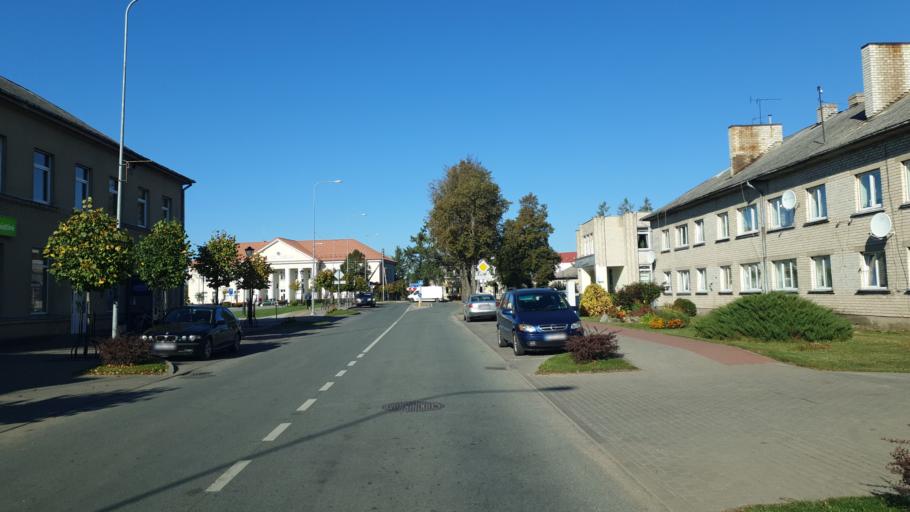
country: LT
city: Varniai
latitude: 55.7417
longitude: 22.3732
